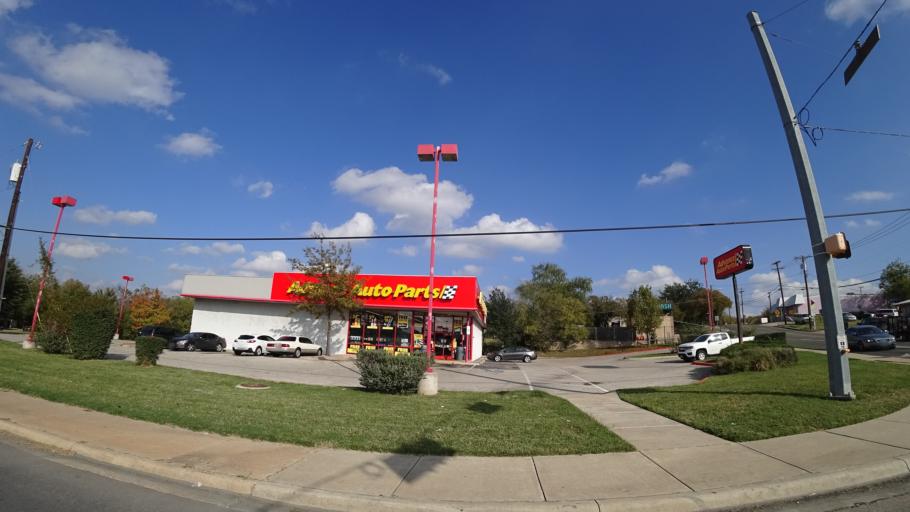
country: US
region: Texas
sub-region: Williamson County
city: Round Rock
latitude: 30.5026
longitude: -97.6765
